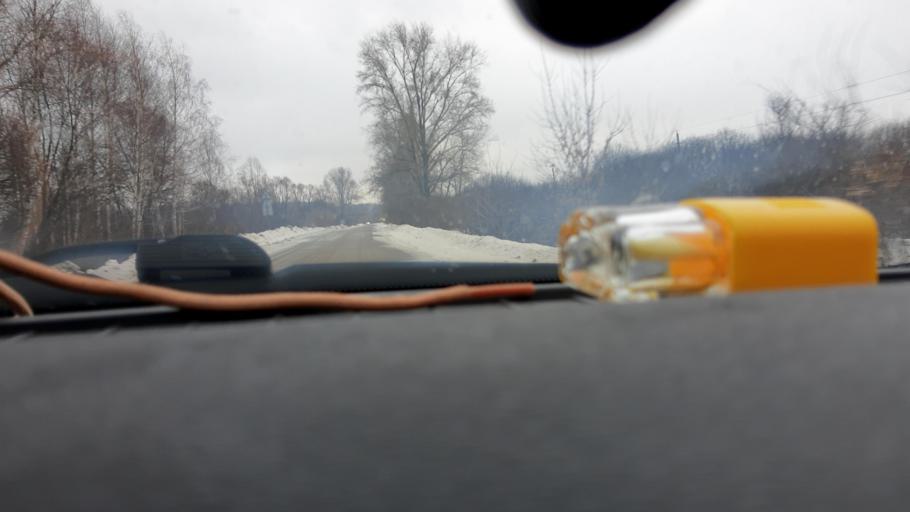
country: RU
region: Bashkortostan
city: Iglino
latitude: 54.6879
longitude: 56.4142
